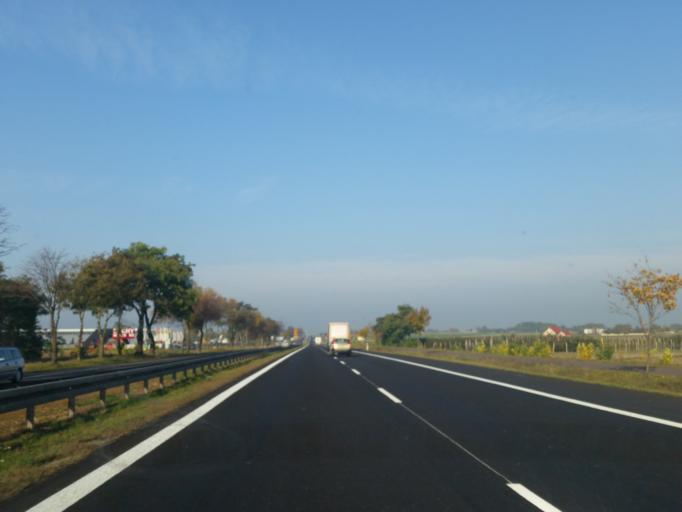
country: PL
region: Masovian Voivodeship
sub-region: Powiat plonski
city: Plonsk
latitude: 52.5935
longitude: 20.4392
